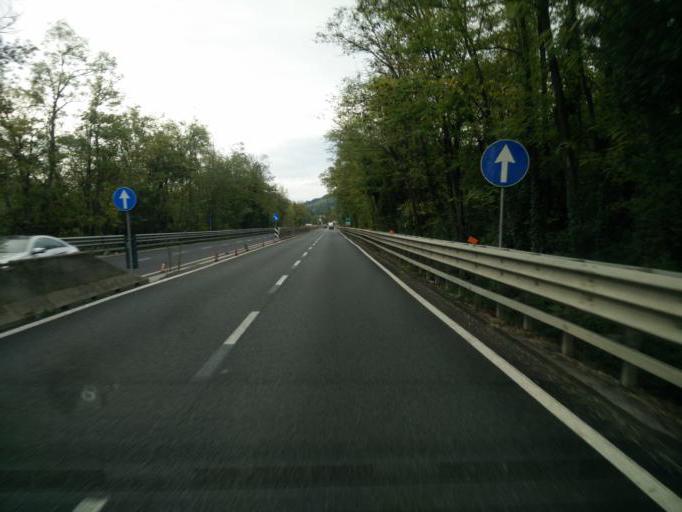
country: IT
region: Tuscany
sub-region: Province of Florence
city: Sambuca
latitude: 43.6084
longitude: 11.1912
